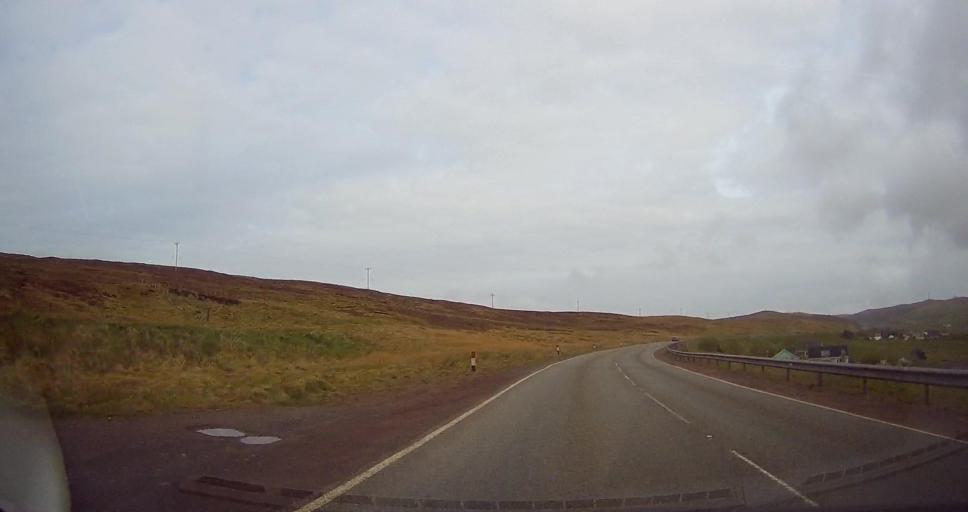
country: GB
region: Scotland
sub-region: Shetland Islands
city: Lerwick
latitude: 60.1223
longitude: -1.2160
